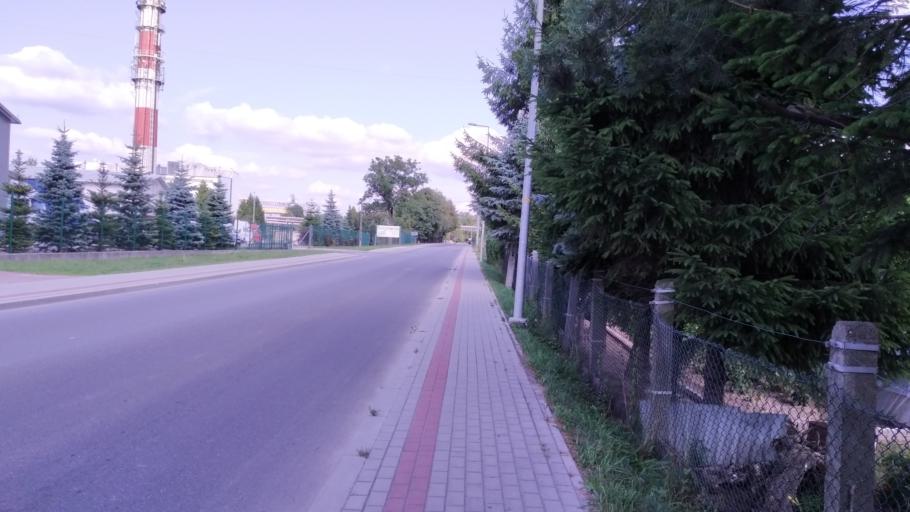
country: PL
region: Subcarpathian Voivodeship
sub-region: Powiat lancucki
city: Lancut
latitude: 50.0787
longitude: 22.2232
